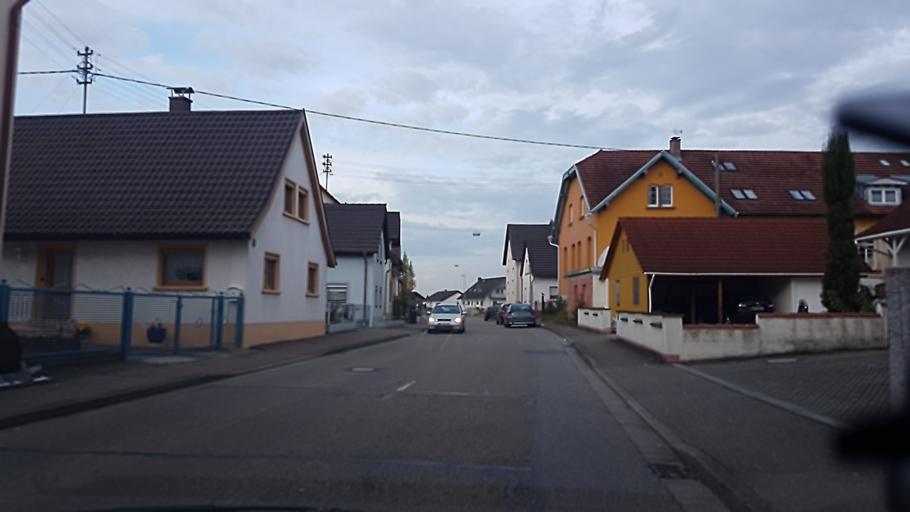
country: DE
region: Baden-Wuerttemberg
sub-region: Freiburg Region
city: Rust
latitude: 48.2407
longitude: 7.7136
